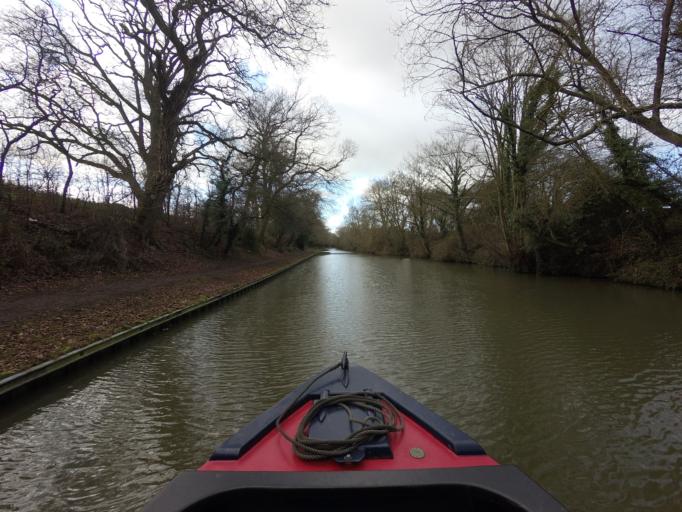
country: GB
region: England
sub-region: Northamptonshire
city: Daventry
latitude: 52.2802
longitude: -1.1477
